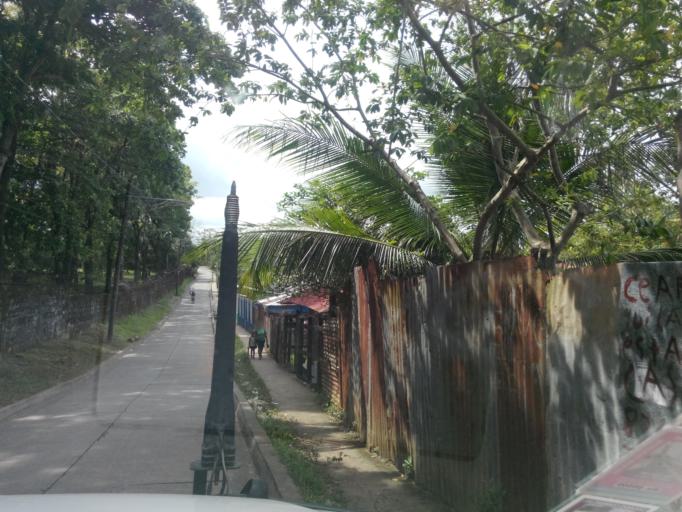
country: NI
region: Atlantico Sur
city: Bluefields
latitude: 12.0096
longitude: -83.7657
